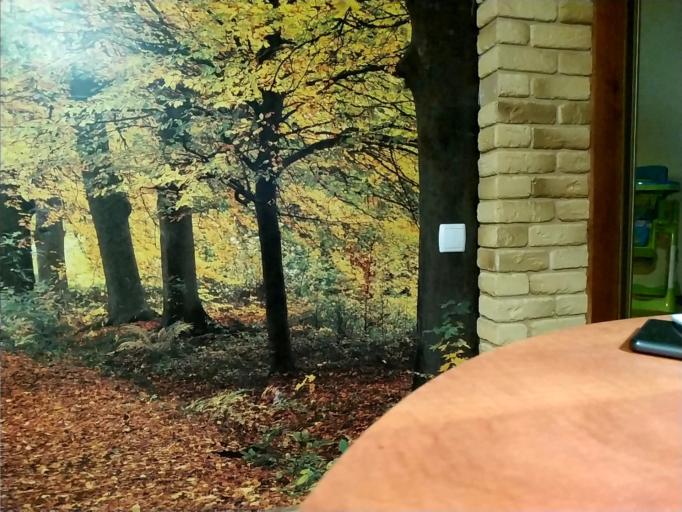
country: BY
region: Minsk
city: Plyeshchanitsy
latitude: 54.4288
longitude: 27.6450
